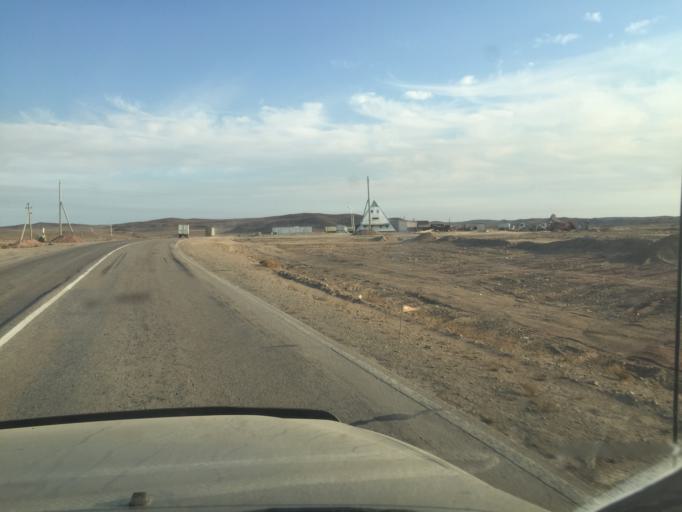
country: KZ
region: Zhambyl
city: Mynaral
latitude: 45.4521
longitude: 73.5997
